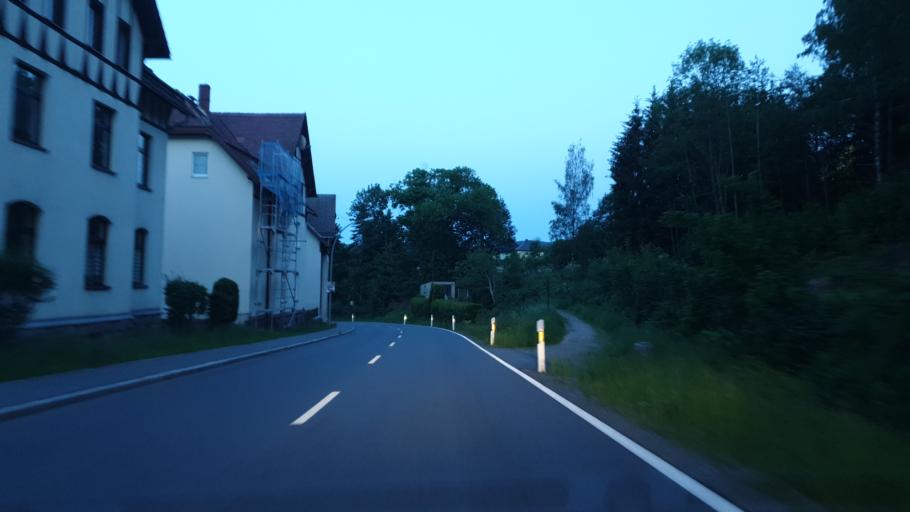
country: DE
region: Saxony
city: Schlema
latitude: 50.5853
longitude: 12.6733
